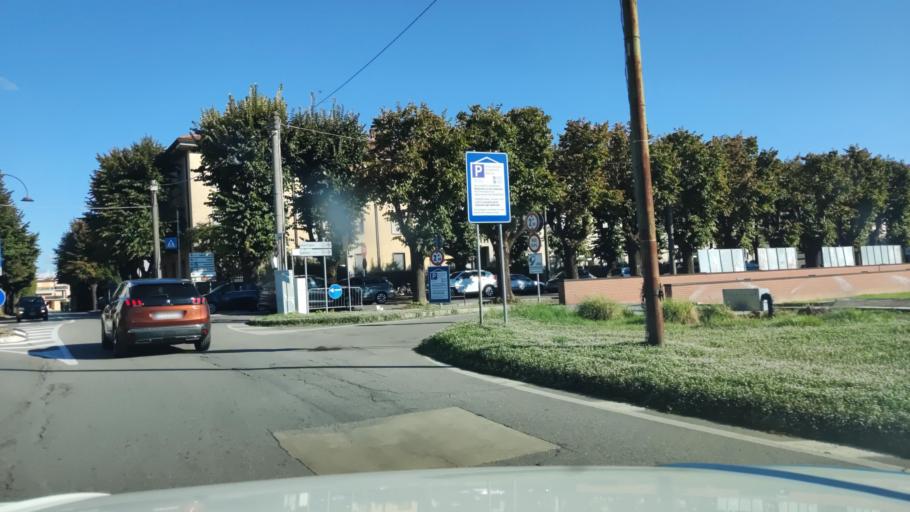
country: IT
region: Lombardy
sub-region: Provincia di Brescia
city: Orzinuovi
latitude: 45.4054
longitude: 9.9255
